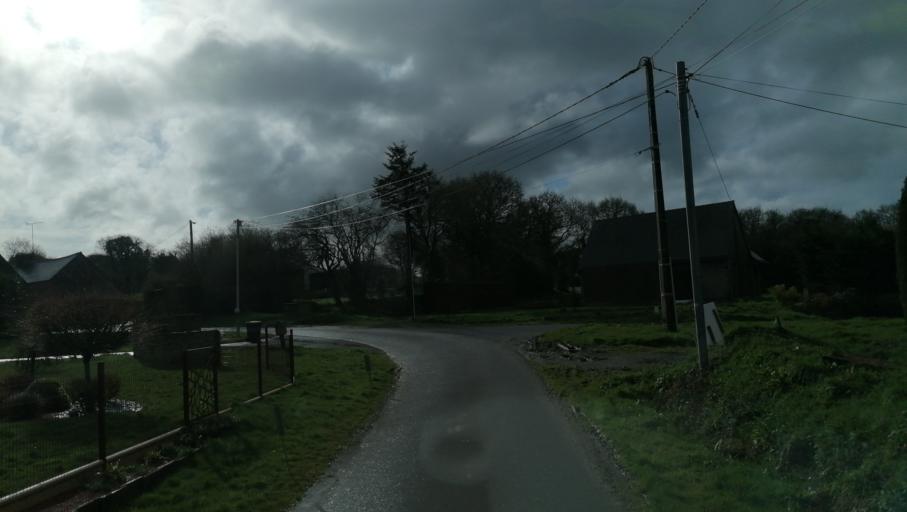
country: FR
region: Brittany
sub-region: Departement des Cotes-d'Armor
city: Lanrodec
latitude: 48.4943
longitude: -3.0323
